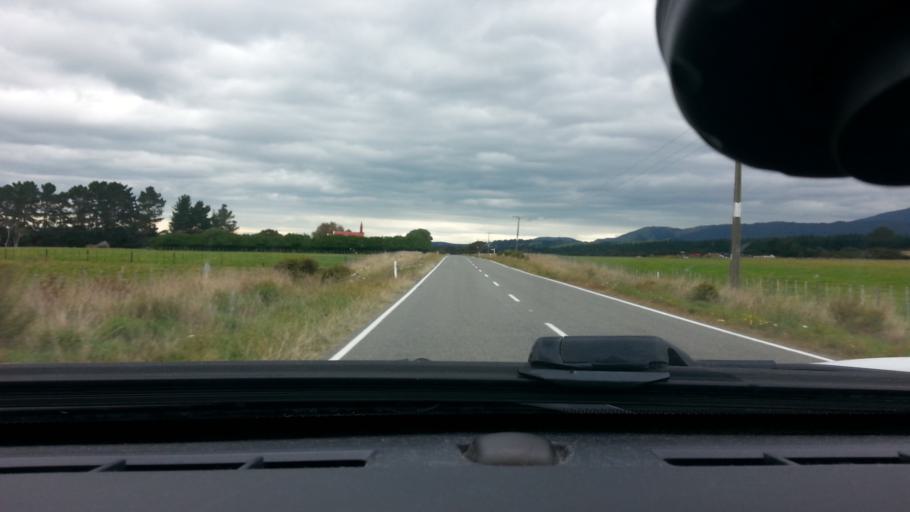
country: NZ
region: Wellington
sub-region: Upper Hutt City
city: Upper Hutt
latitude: -41.3293
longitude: 175.2366
